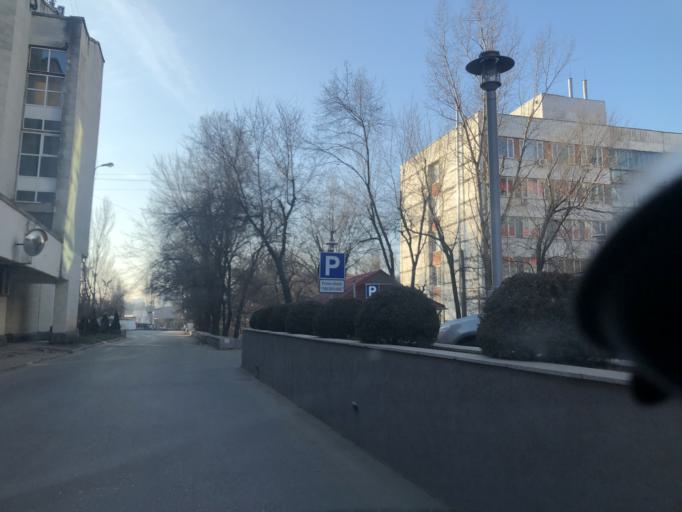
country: MD
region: Chisinau
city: Chisinau
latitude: 47.0336
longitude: 28.8549
